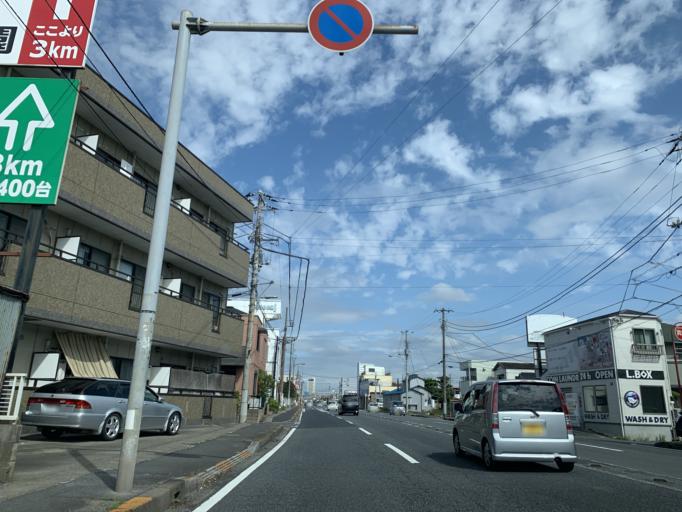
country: JP
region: Tokyo
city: Urayasu
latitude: 35.6947
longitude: 139.9233
